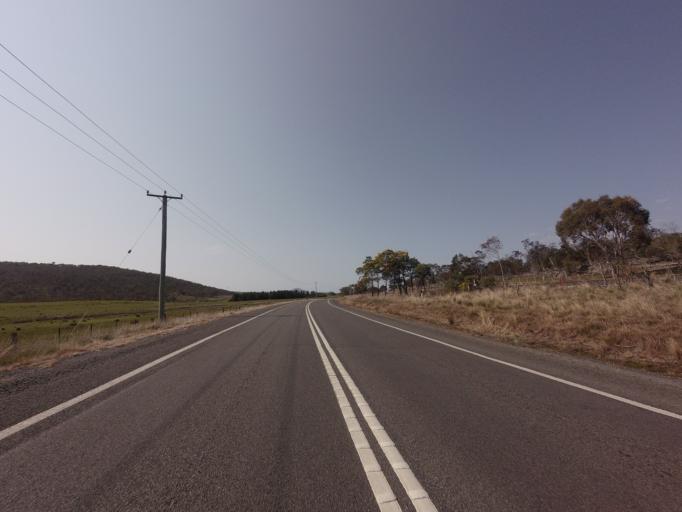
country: AU
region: Tasmania
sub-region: Northern Midlands
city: Evandale
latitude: -41.8100
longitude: 147.5951
